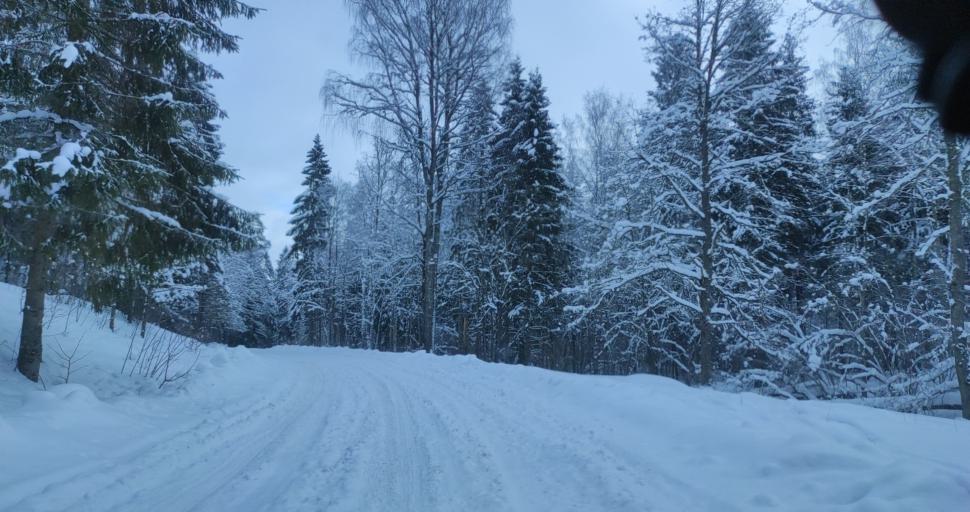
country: LV
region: Vecpiebalga
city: Vecpiebalga
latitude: 56.8710
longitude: 25.9666
